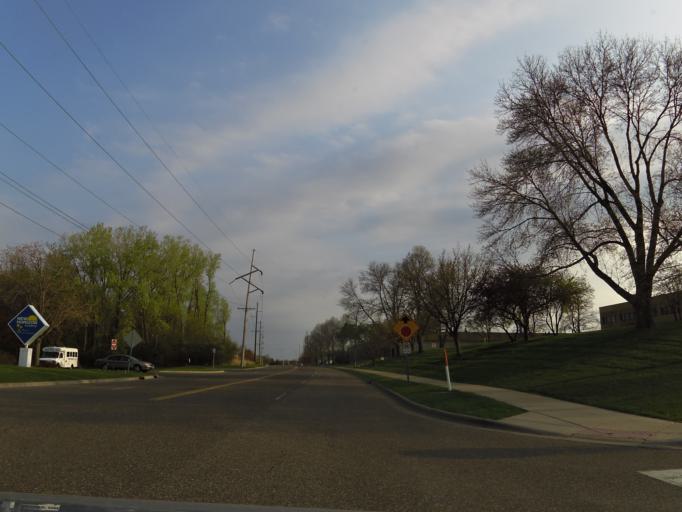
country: US
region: Minnesota
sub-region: Ramsey County
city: Maplewood
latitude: 44.9592
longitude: -92.9927
